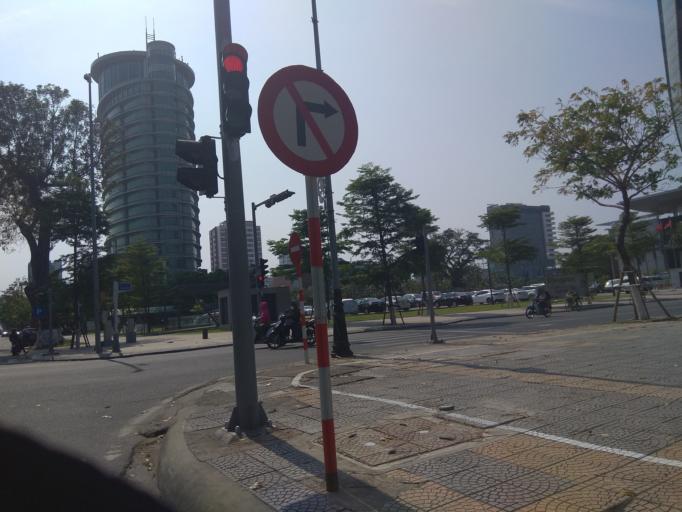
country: VN
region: Da Nang
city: Da Nang
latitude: 16.0756
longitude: 108.2236
